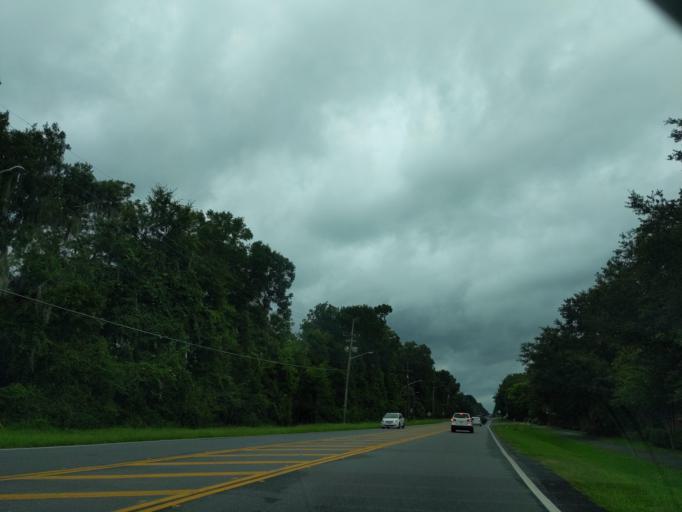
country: US
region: Florida
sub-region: Alachua County
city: Gainesville
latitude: 29.6026
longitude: -82.4226
